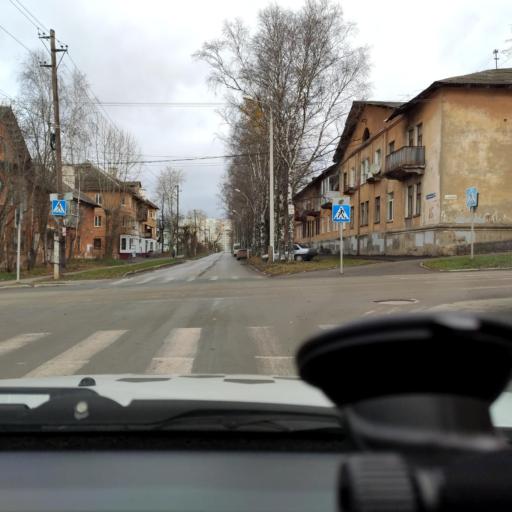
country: RU
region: Perm
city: Kondratovo
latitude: 57.9728
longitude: 56.1750
